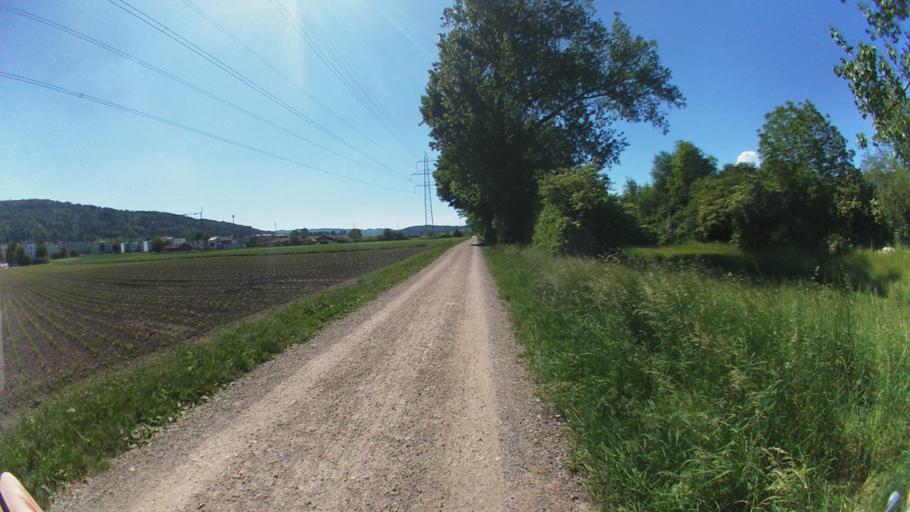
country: CH
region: Zurich
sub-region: Bezirk Dielsdorf
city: Daenikon
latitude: 47.4505
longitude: 8.4094
